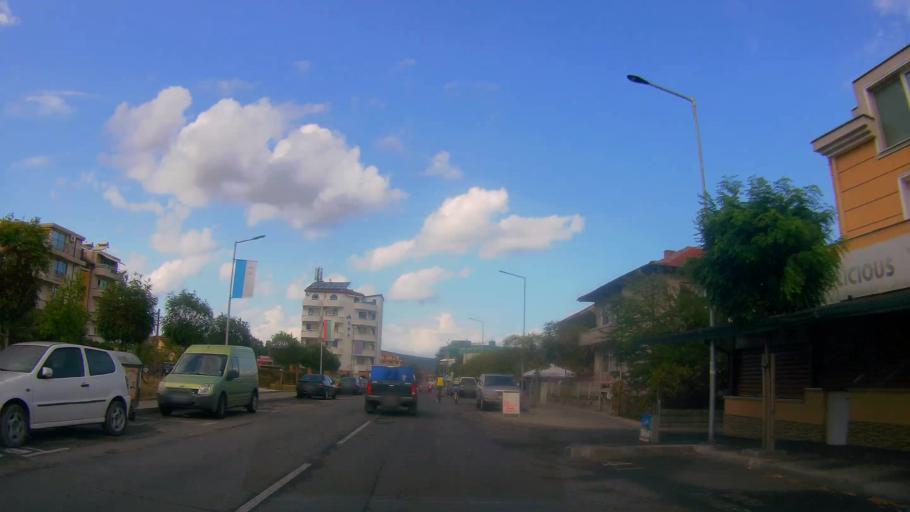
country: BG
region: Burgas
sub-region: Obshtina Primorsko
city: Primorsko
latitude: 42.2699
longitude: 27.7502
